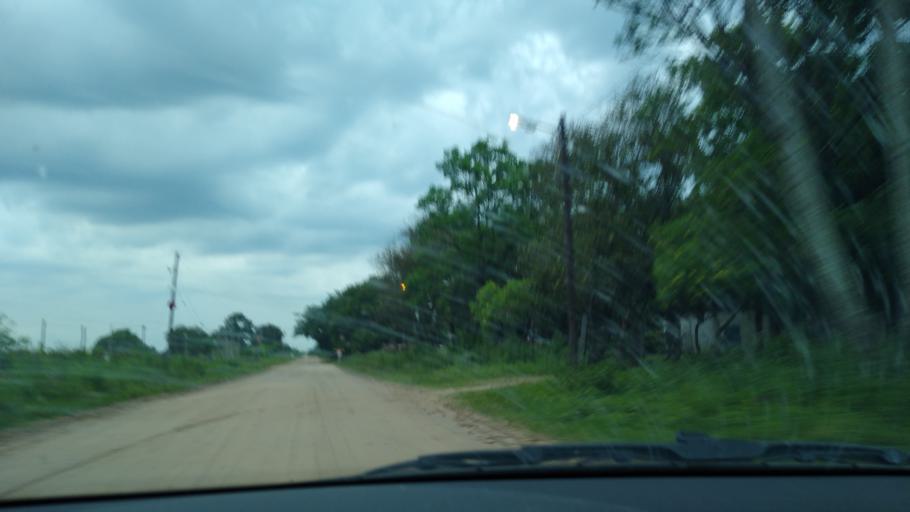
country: AR
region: Chaco
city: Puerto Vilelas
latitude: -27.5136
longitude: -58.9705
